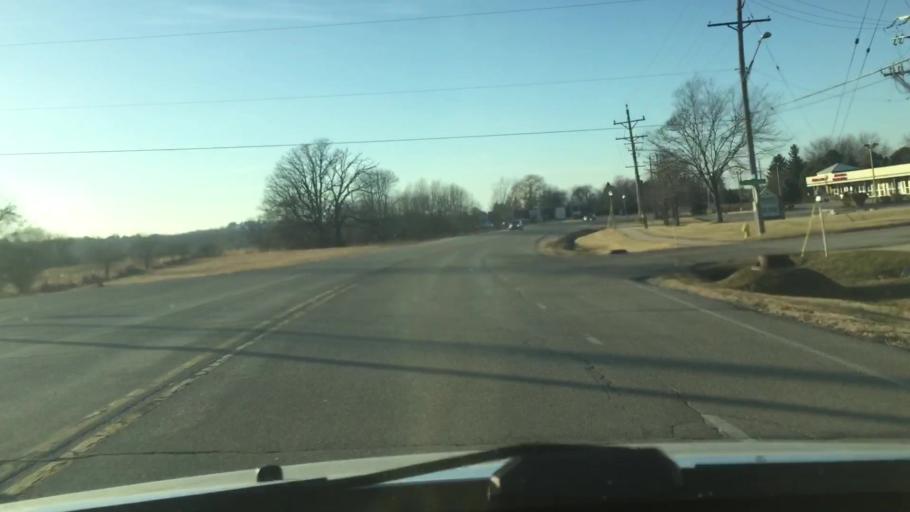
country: US
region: Wisconsin
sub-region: Waukesha County
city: Sussex
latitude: 43.1340
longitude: -88.2360
